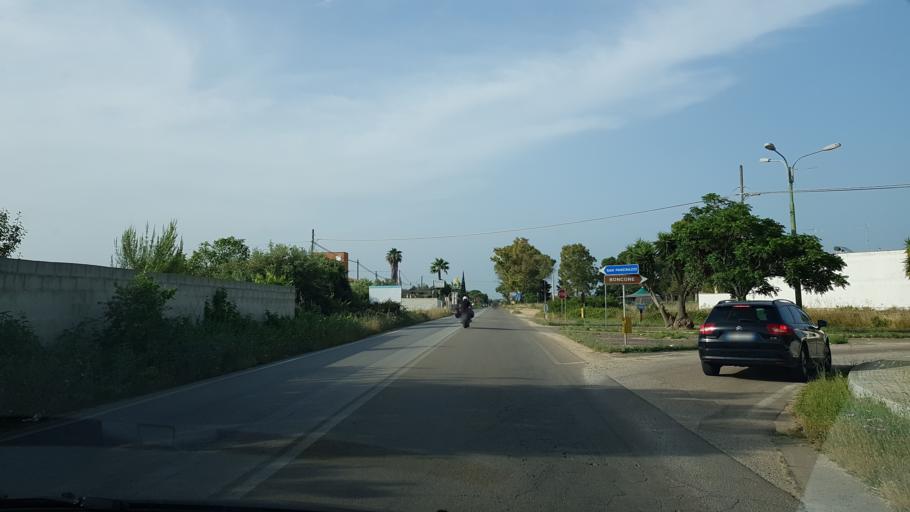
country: IT
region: Apulia
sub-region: Provincia di Lecce
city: Porto Cesareo
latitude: 40.2978
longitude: 17.8568
